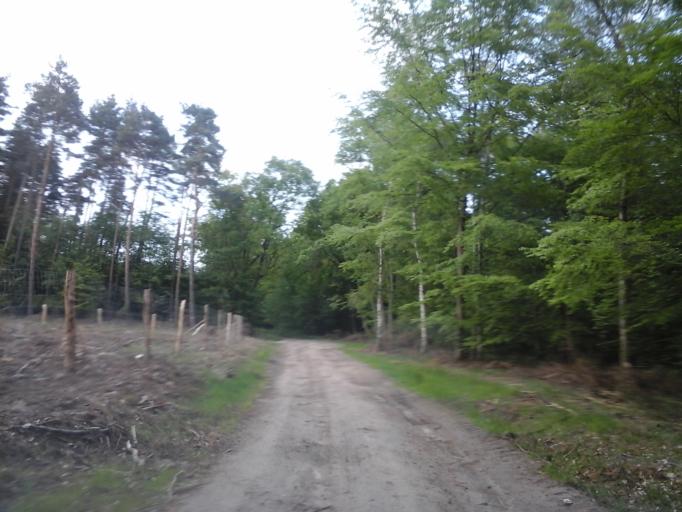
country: PL
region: West Pomeranian Voivodeship
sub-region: Powiat choszczenski
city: Pelczyce
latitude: 52.9540
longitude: 15.3564
